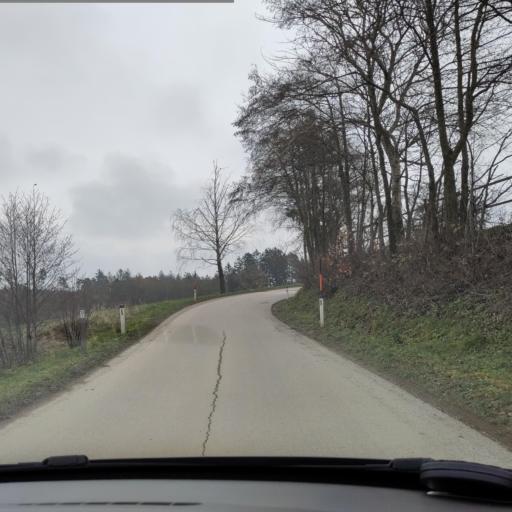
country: AT
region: Lower Austria
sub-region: Politischer Bezirk Sankt Polten
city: Hafnerbach
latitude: 48.2590
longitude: 15.5033
